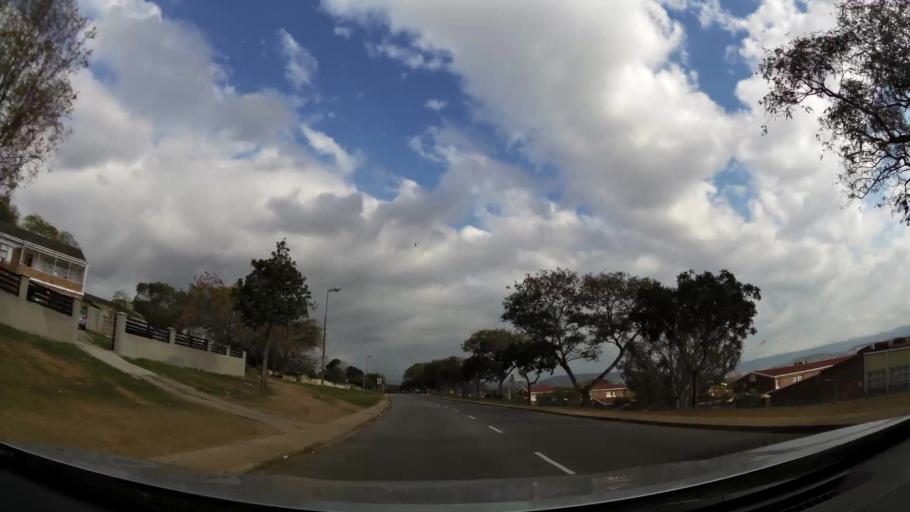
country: ZA
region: Eastern Cape
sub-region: Nelson Mandela Bay Metropolitan Municipality
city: Uitenhage
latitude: -33.7384
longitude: 25.4045
